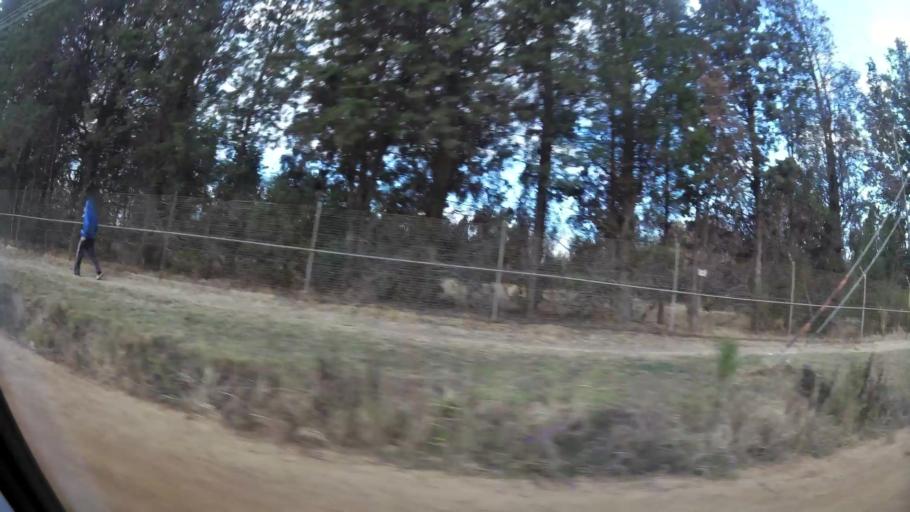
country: ZA
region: Gauteng
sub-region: City of Johannesburg Metropolitan Municipality
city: Diepsloot
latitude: -25.9925
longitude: 27.9897
